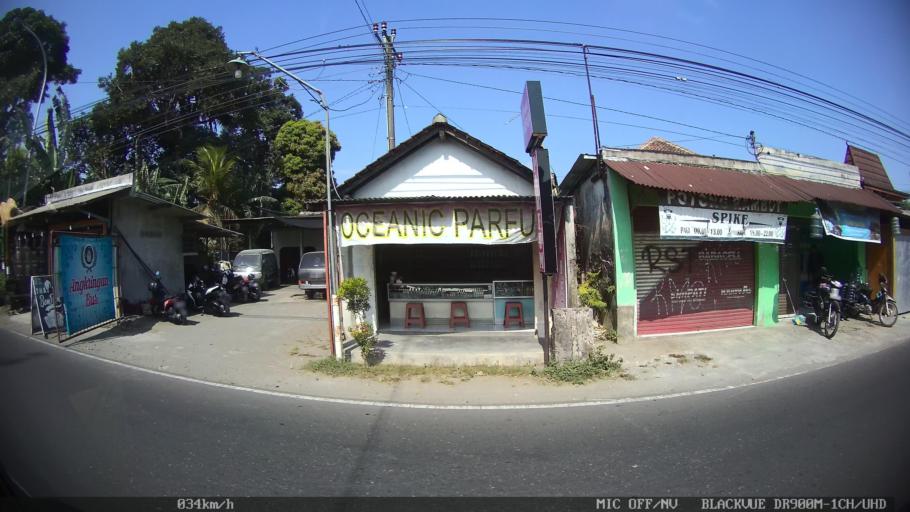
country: ID
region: Daerah Istimewa Yogyakarta
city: Sewon
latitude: -7.8791
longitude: 110.3904
